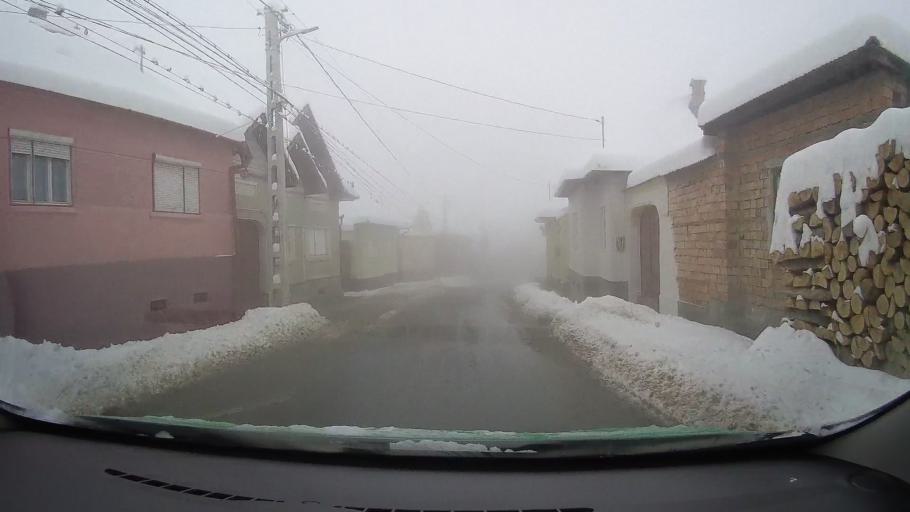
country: RO
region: Sibiu
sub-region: Comuna Poiana Sibiului
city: Poiana Sibiului
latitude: 45.8019
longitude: 23.7183
